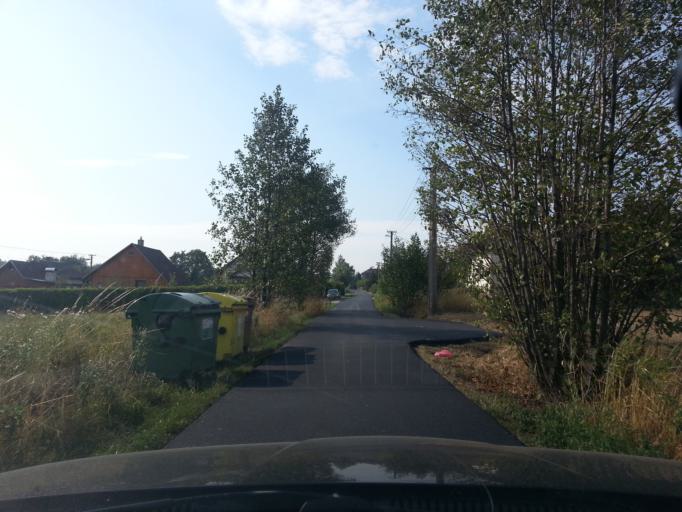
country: CZ
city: Detmarovice
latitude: 49.8898
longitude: 18.4440
